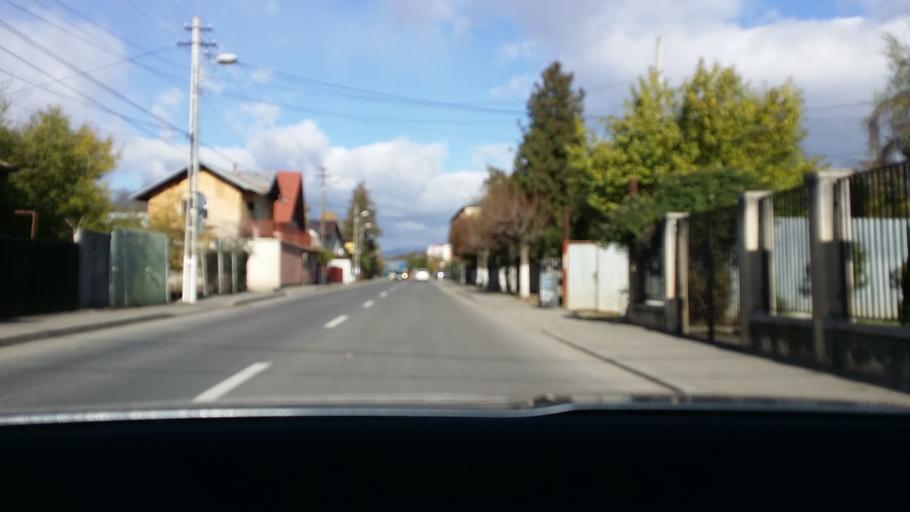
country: RO
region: Prahova
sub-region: Municipiul Campina
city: Campina
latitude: 45.1268
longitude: 25.7525
